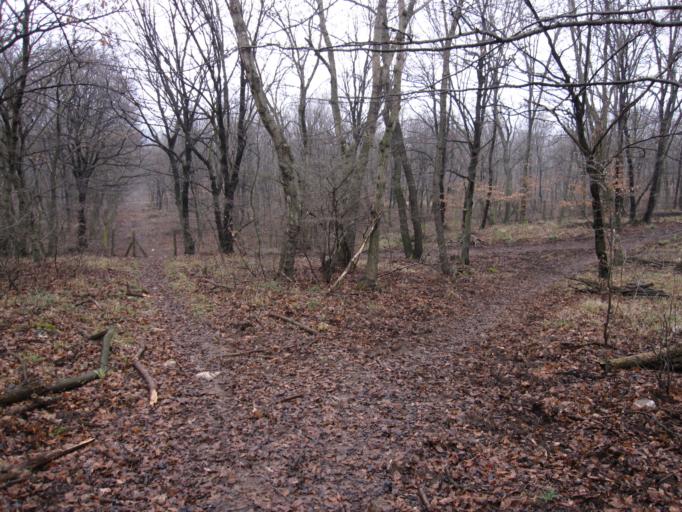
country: HU
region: Pest
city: Piliscsaba
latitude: 47.6494
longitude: 18.8395
